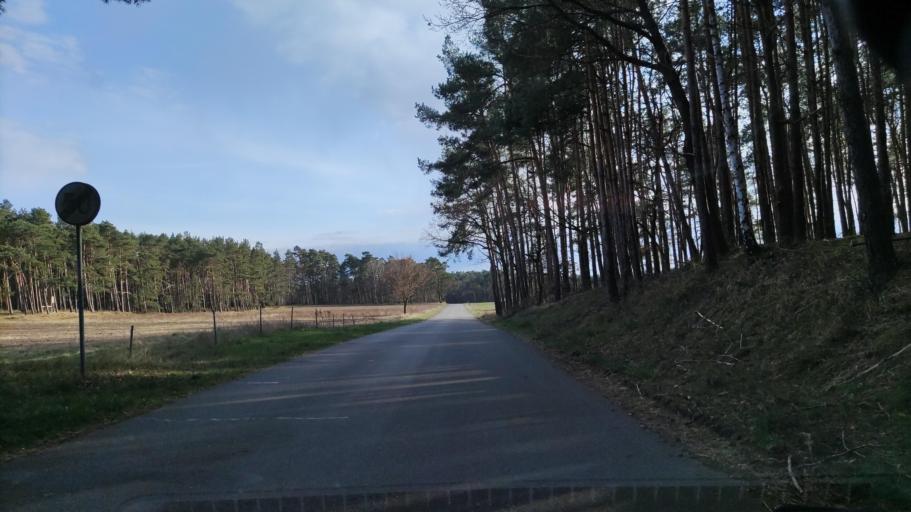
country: DE
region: Lower Saxony
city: Klein Gusborn
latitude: 53.0868
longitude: 11.2227
